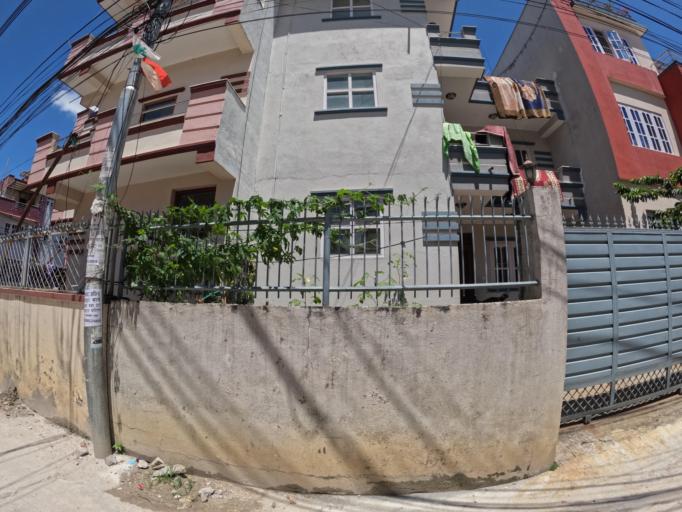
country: NP
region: Central Region
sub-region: Bagmati Zone
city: Kathmandu
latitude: 27.7505
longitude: 85.3298
